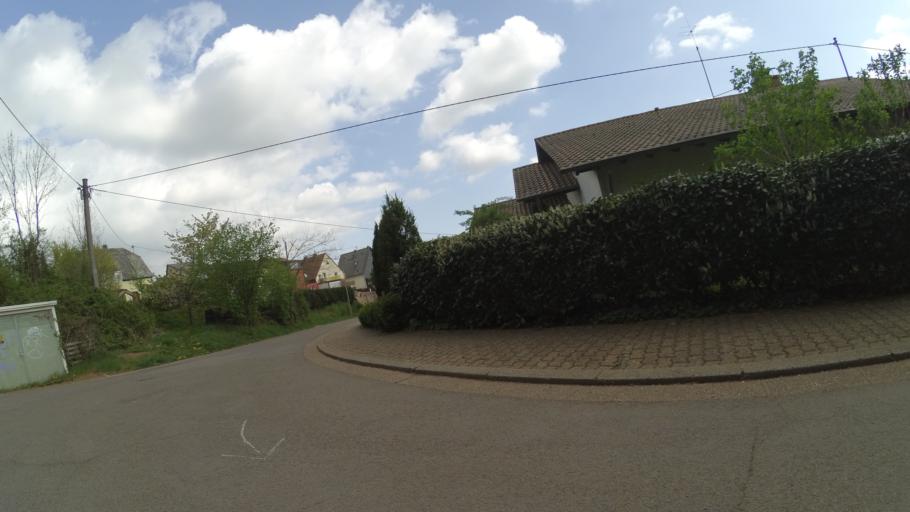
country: DE
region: Saarland
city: Wadern
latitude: 49.5370
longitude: 6.8856
